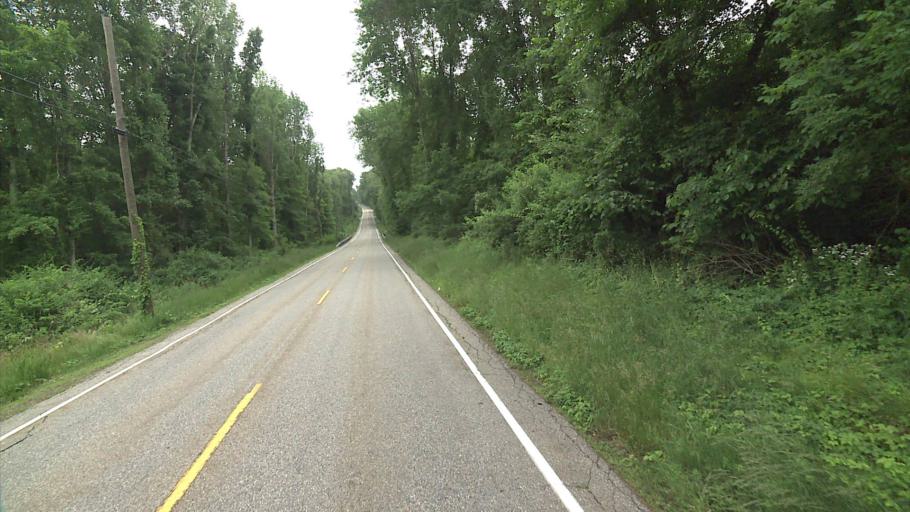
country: US
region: Connecticut
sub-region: Tolland County
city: Hebron
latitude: 41.7127
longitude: -72.3685
